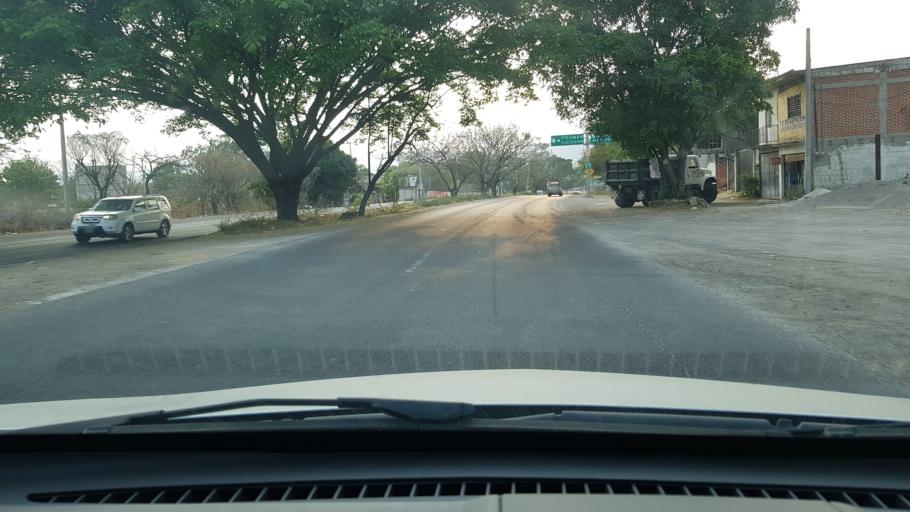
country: MX
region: Morelos
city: Yautepec
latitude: 18.8701
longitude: -99.0643
